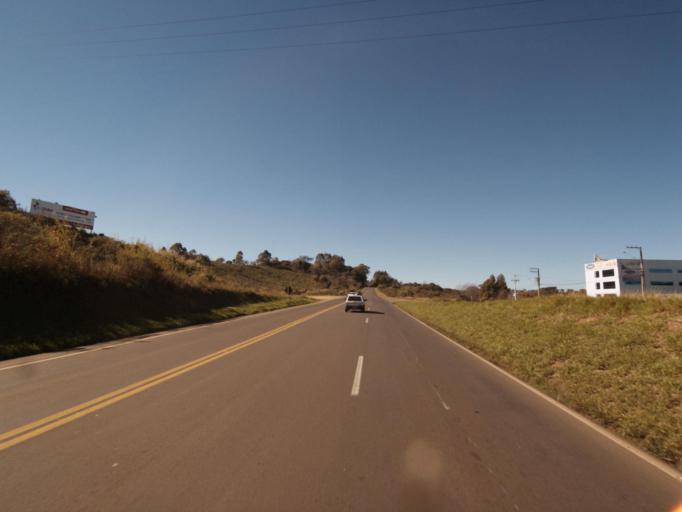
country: BR
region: Santa Catarina
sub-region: Chapeco
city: Chapeco
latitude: -26.9658
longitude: -52.5543
